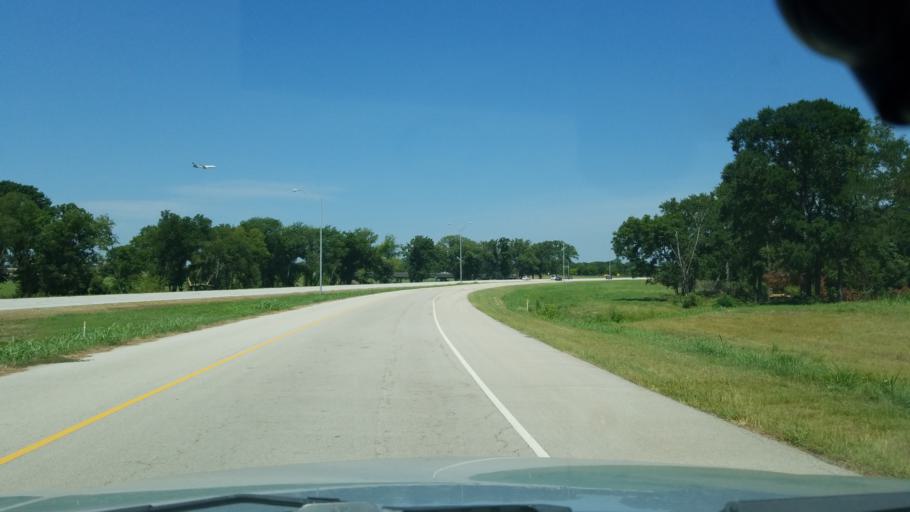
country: US
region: Texas
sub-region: Tarrant County
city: Euless
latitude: 32.8383
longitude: -97.0347
